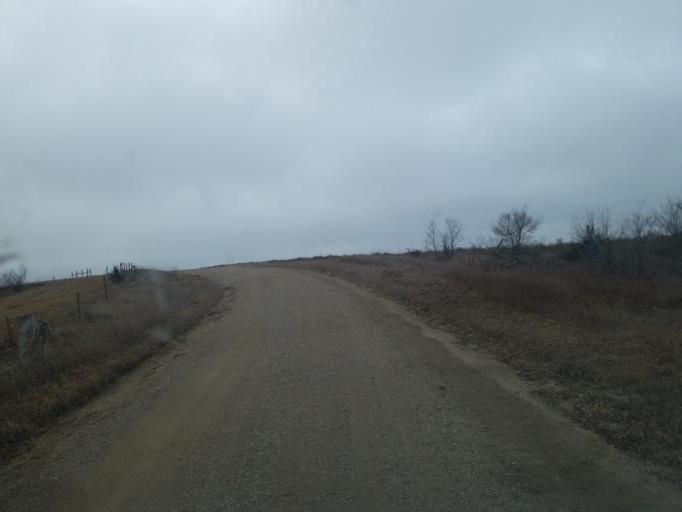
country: US
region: Nebraska
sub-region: Knox County
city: Center
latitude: 42.5465
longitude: -97.8007
